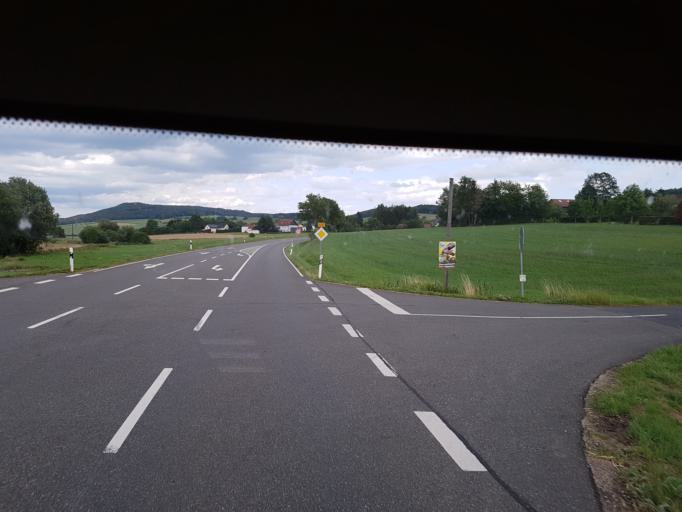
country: DE
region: Rheinland-Pfalz
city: Budesheim
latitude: 50.2185
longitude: 6.5539
